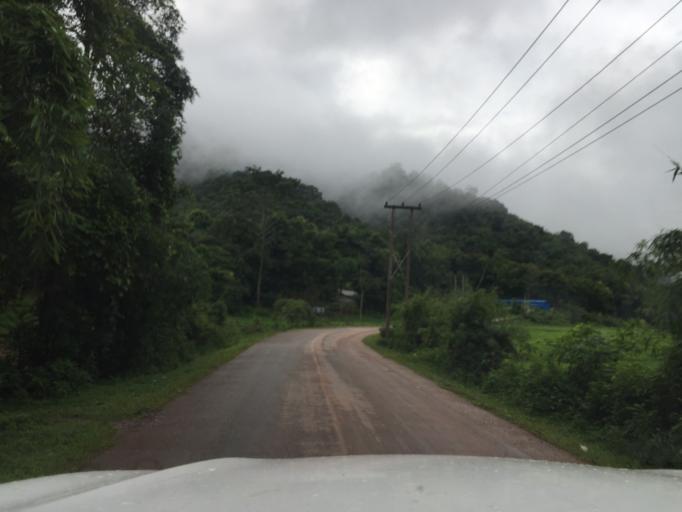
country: LA
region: Oudomxai
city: Muang La
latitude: 20.8392
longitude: 102.1028
